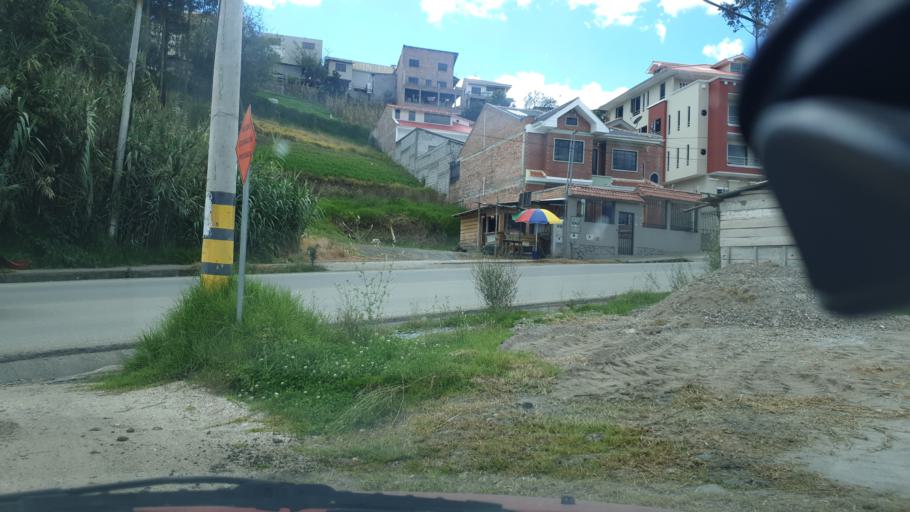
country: EC
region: Azuay
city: Cuenca
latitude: -2.9322
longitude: -78.9680
